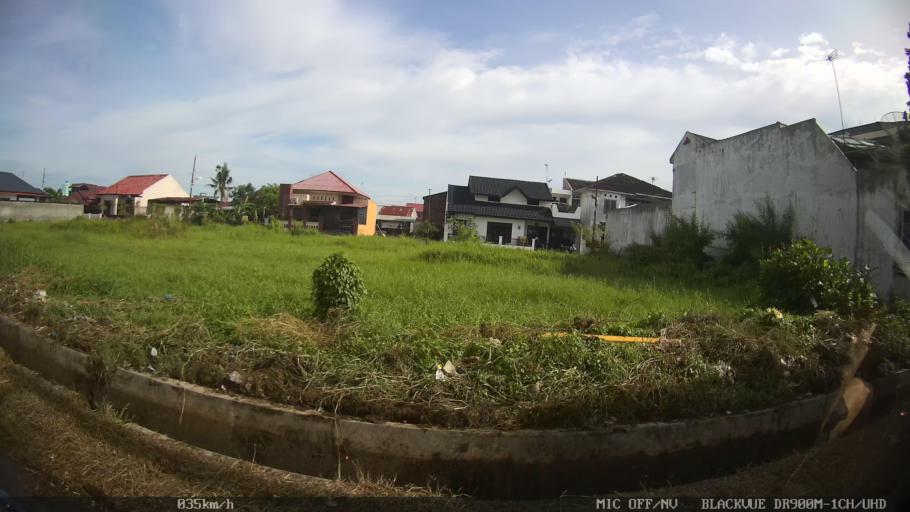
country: ID
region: North Sumatra
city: Medan
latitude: 3.6114
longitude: 98.6569
